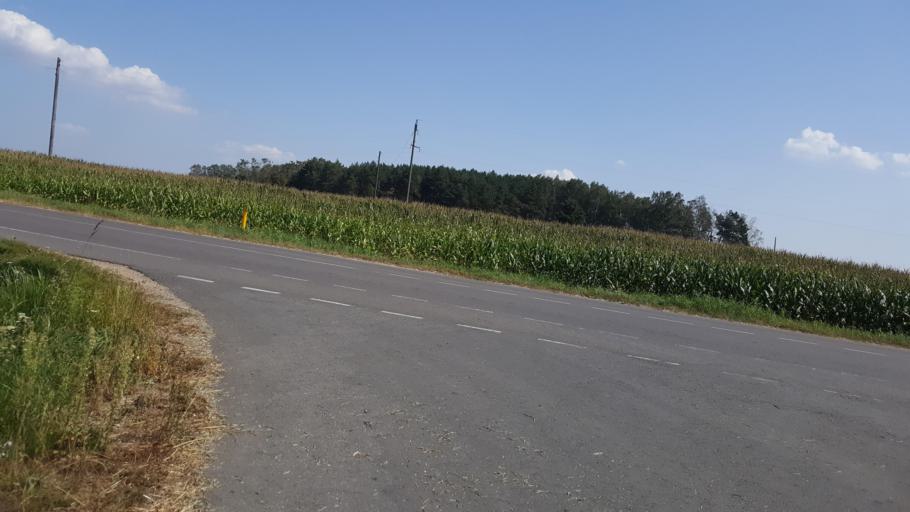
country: PL
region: Podlasie
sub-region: Powiat hajnowski
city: Czeremcha
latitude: 52.4893
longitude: 23.5511
